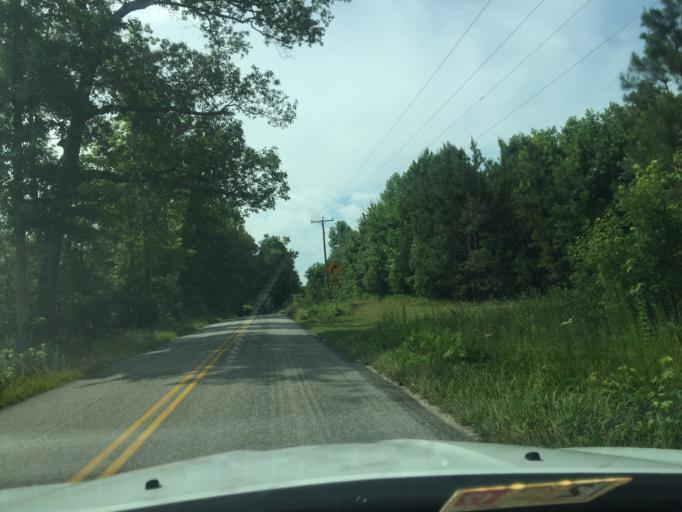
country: US
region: Virginia
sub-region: Charles City County
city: Charles City
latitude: 37.3782
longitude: -77.0051
